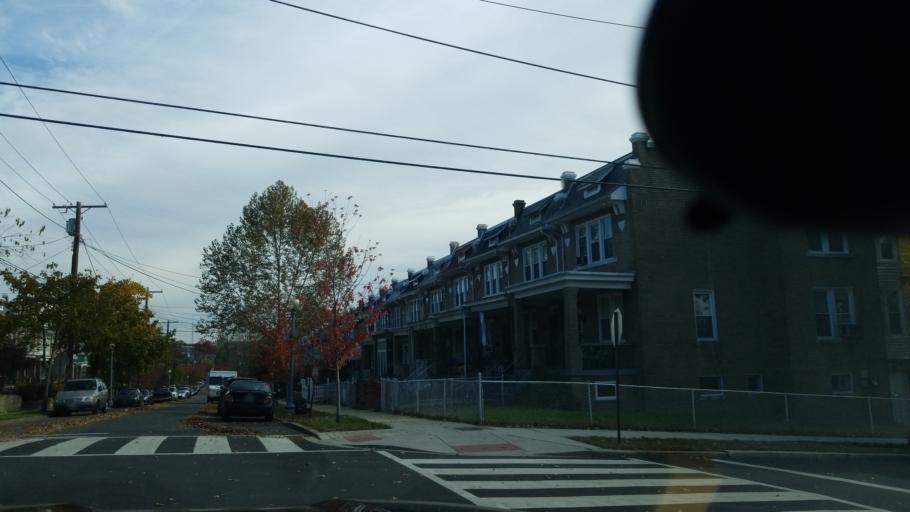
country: US
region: Maryland
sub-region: Montgomery County
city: Takoma Park
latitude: 38.9542
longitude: -77.0178
